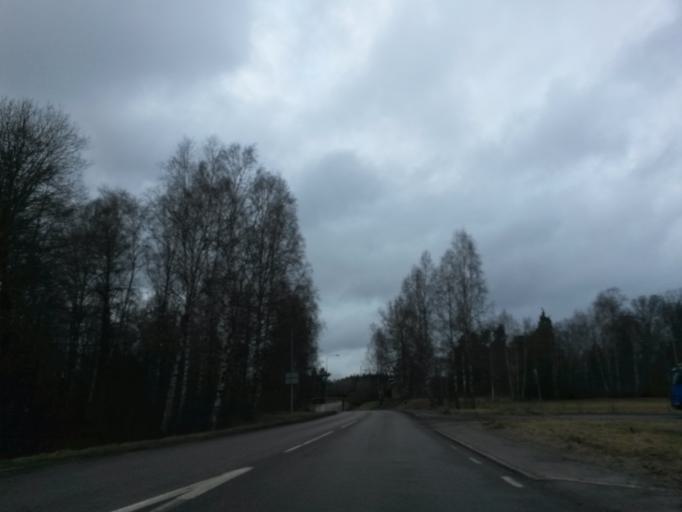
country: SE
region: Vaestra Goetaland
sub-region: Herrljunga Kommun
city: Herrljunga
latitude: 58.0824
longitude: 13.0441
